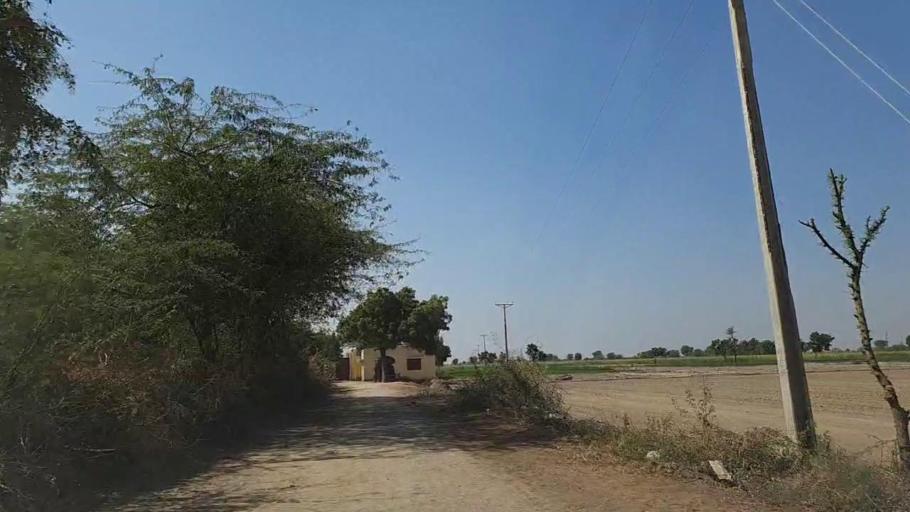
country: PK
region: Sindh
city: Samaro
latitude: 25.3949
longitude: 69.3835
